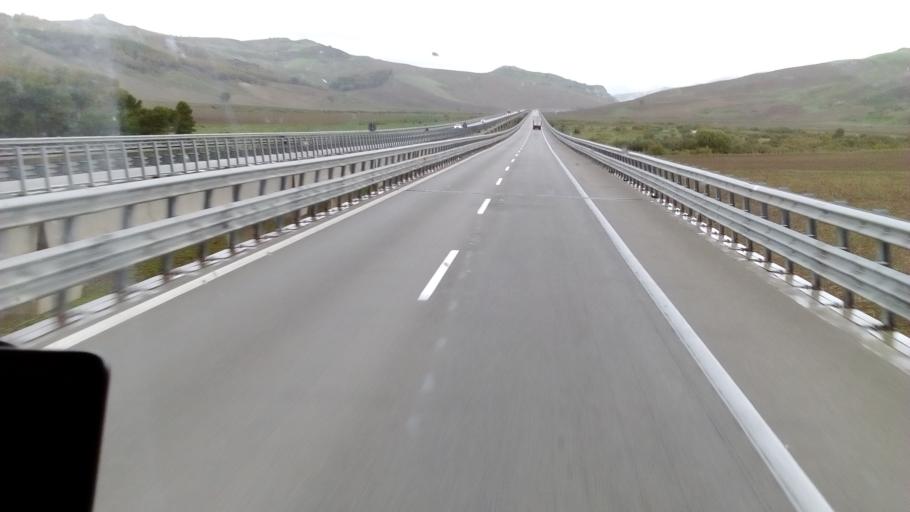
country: IT
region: Sicily
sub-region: Enna
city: Villarosa
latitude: 37.5544
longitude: 14.1410
